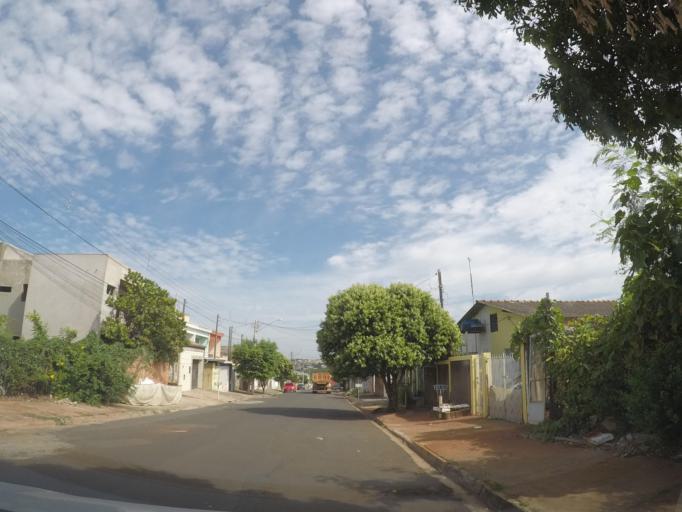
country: BR
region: Sao Paulo
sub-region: Hortolandia
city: Hortolandia
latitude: -22.8292
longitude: -47.1906
